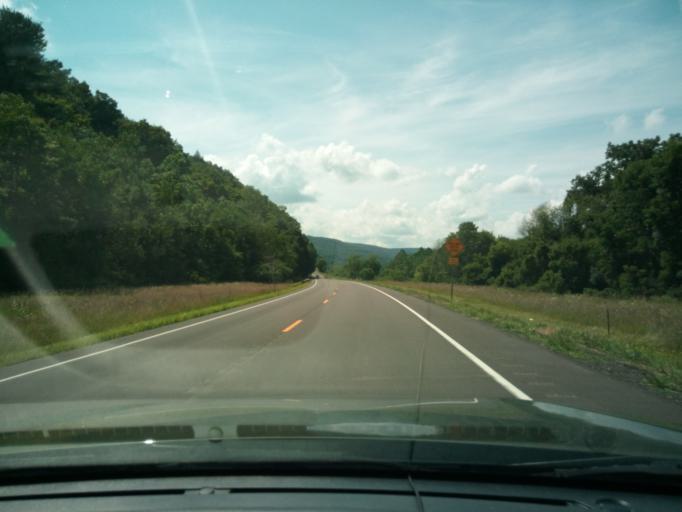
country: US
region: New York
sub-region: Chemung County
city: Southport
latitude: 42.0162
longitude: -76.7071
